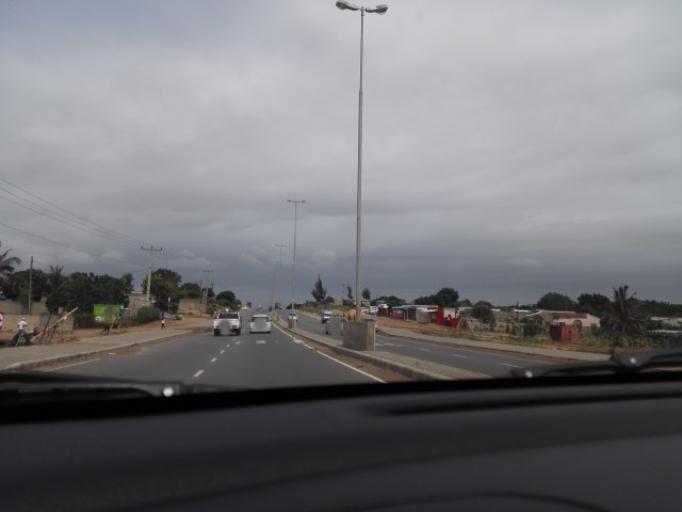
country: MZ
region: Maputo City
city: Maputo
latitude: -25.8243
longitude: 32.5946
